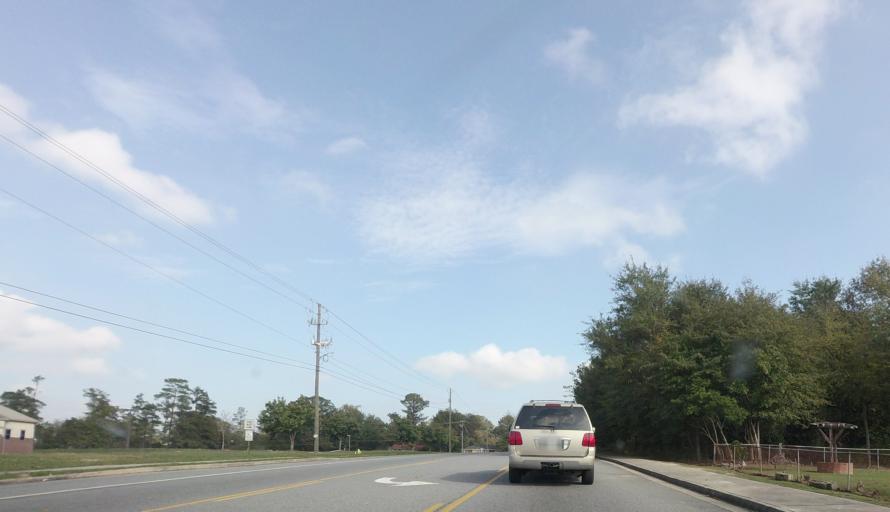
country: US
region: Georgia
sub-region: Bibb County
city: Macon
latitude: 32.8060
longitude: -83.6731
